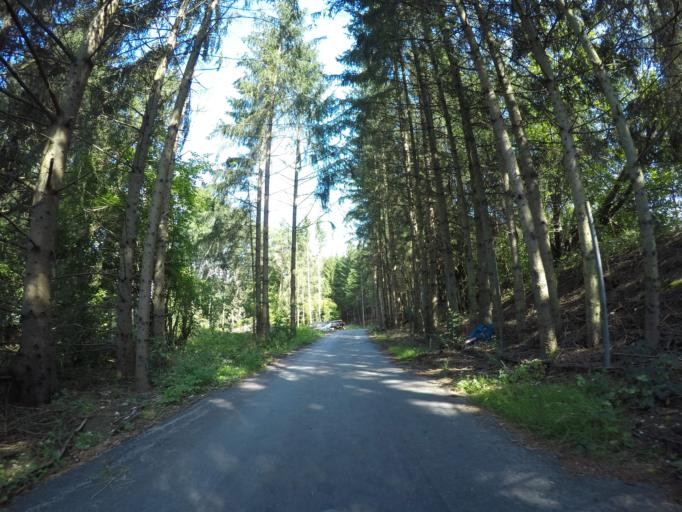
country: DE
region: Baden-Wuerttemberg
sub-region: Tuebingen Region
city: Eningen unter Achalm
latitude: 48.5149
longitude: 9.2421
